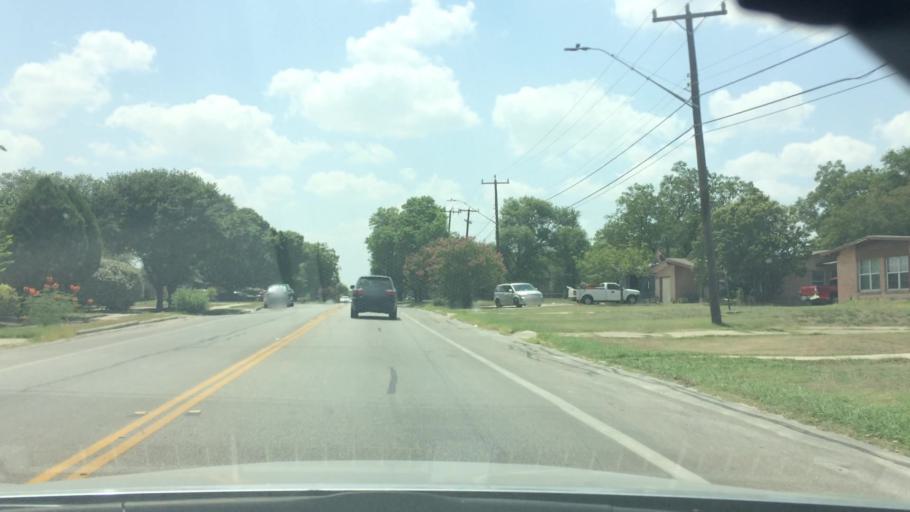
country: US
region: Texas
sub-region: Bexar County
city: Olmos Park
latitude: 29.5043
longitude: -98.4845
